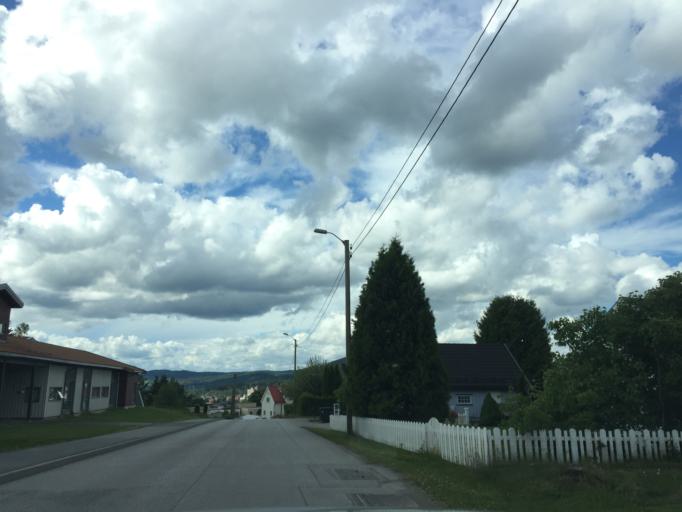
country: NO
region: Hedmark
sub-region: Kongsvinger
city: Kongsvinger
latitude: 60.1815
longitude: 12.0127
